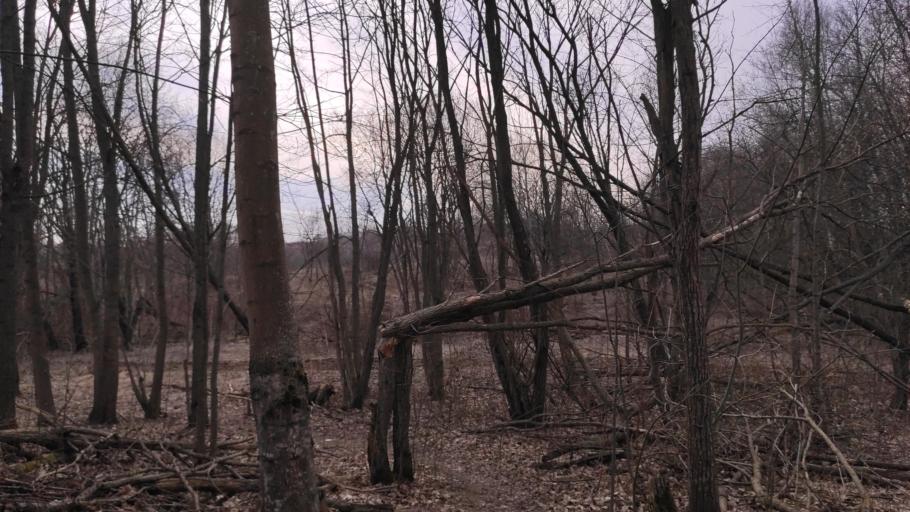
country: BY
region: Minsk
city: Novoye Medvezhino
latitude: 53.8869
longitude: 27.4670
